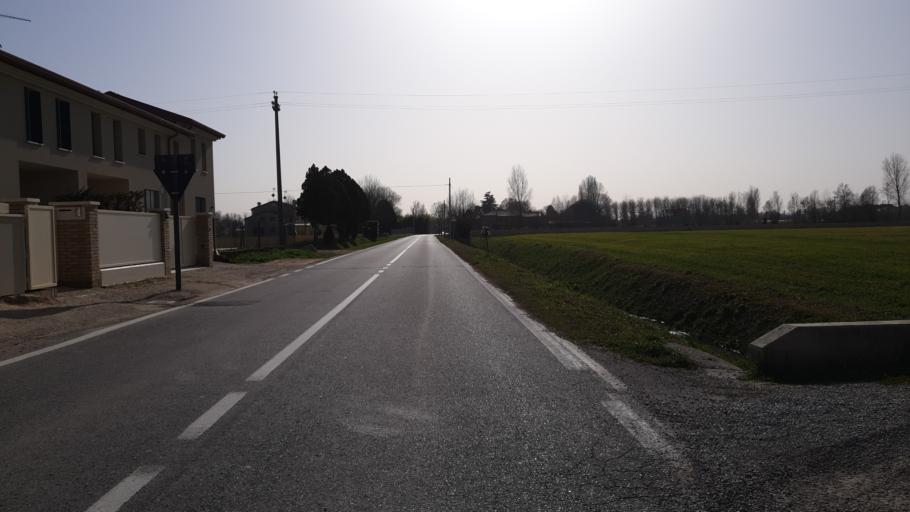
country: IT
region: Veneto
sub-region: Provincia di Padova
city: Saletto
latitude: 45.4845
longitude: 11.8821
